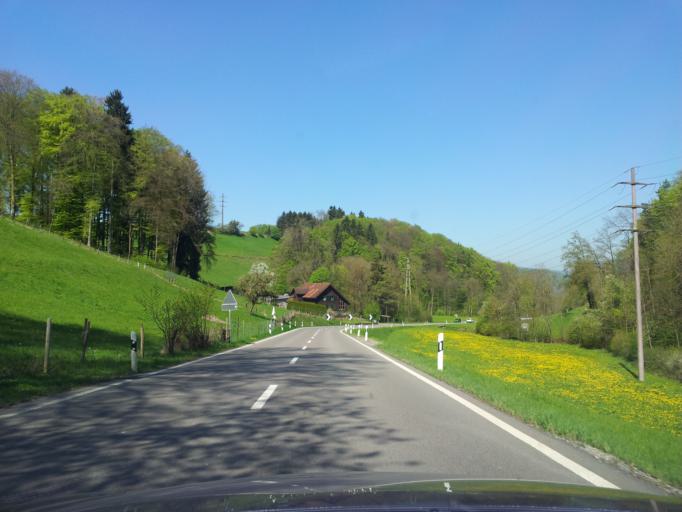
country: CH
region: Zurich
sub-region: Bezirk Dietikon
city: Birmensdorf
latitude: 47.3445
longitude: 8.4486
